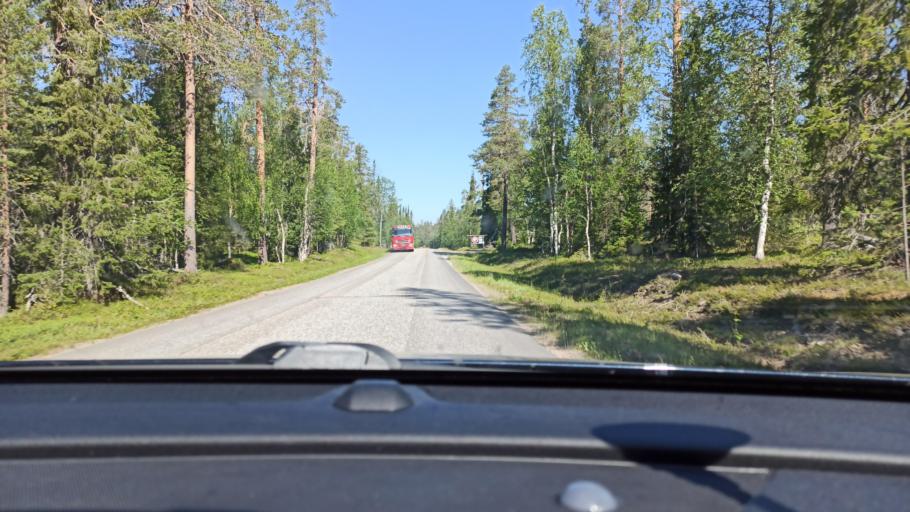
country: FI
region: Lapland
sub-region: Tunturi-Lappi
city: Kolari
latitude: 67.6646
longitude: 24.1620
